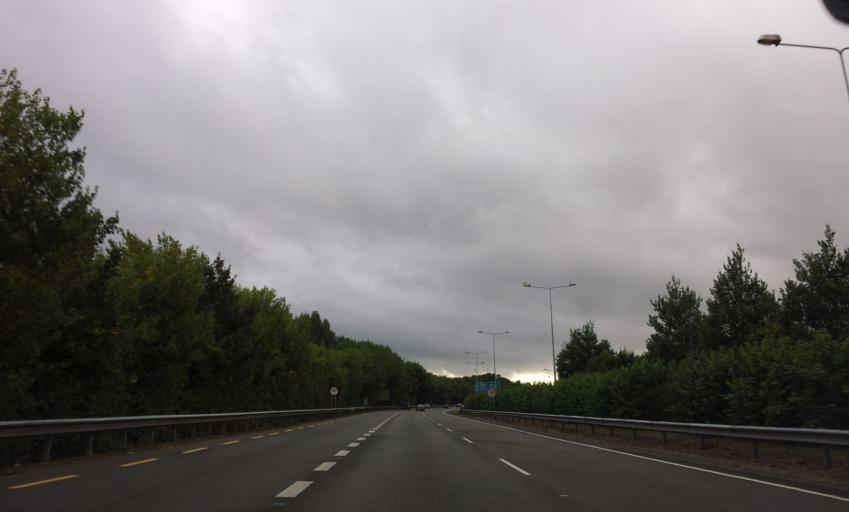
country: IE
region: Munster
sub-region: County Cork
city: Passage West
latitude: 51.9045
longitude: -8.3726
